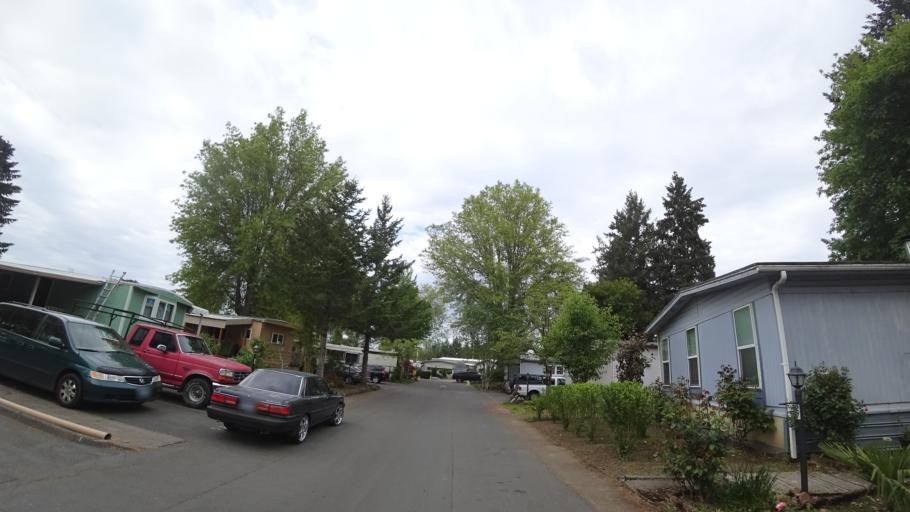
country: US
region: Oregon
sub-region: Washington County
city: Hillsboro
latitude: 45.5003
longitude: -122.9522
